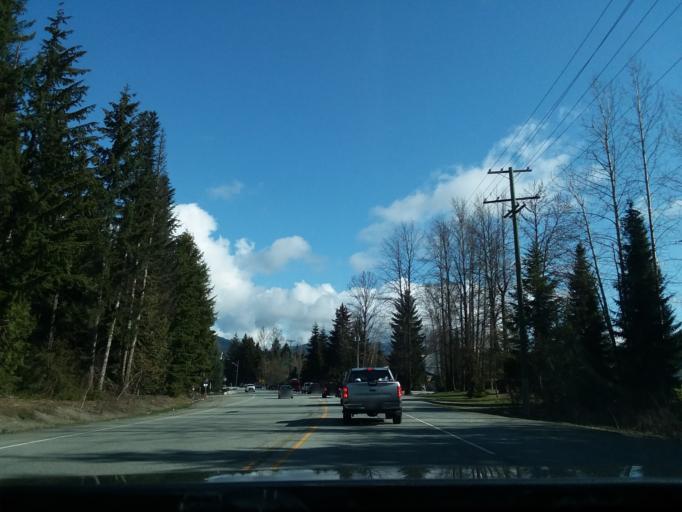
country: CA
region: British Columbia
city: Whistler
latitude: 50.1130
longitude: -122.9595
